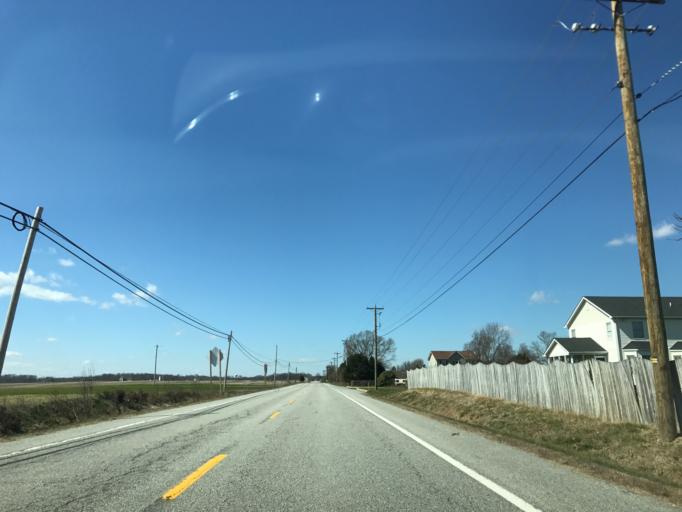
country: US
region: Maryland
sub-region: Queen Anne's County
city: Centreville
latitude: 39.0299
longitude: -76.0388
